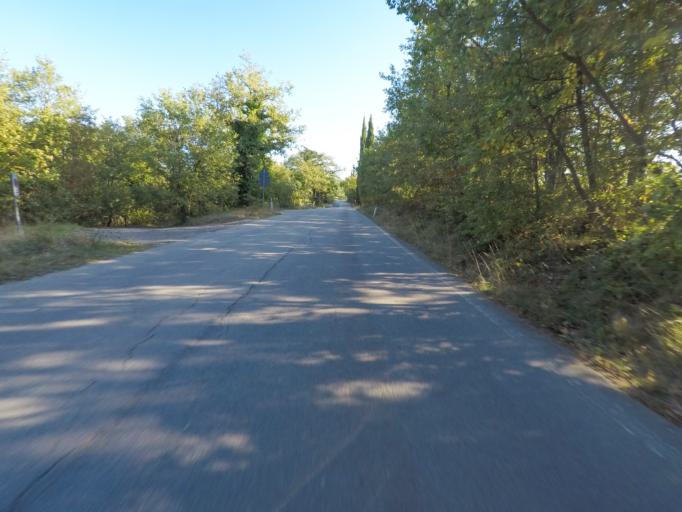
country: IT
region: Tuscany
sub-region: Provincia di Siena
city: Gaiole in Chianti
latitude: 43.4432
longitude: 11.3941
